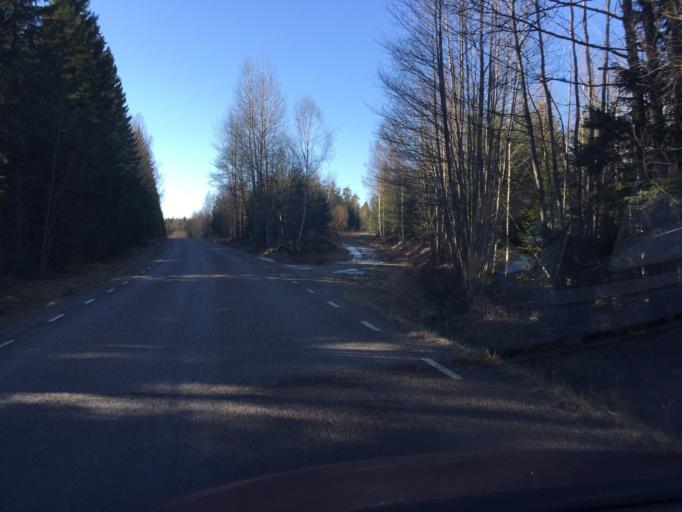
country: SE
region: OErebro
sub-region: Orebro Kommun
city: Odensbacken
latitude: 59.0201
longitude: 15.6193
